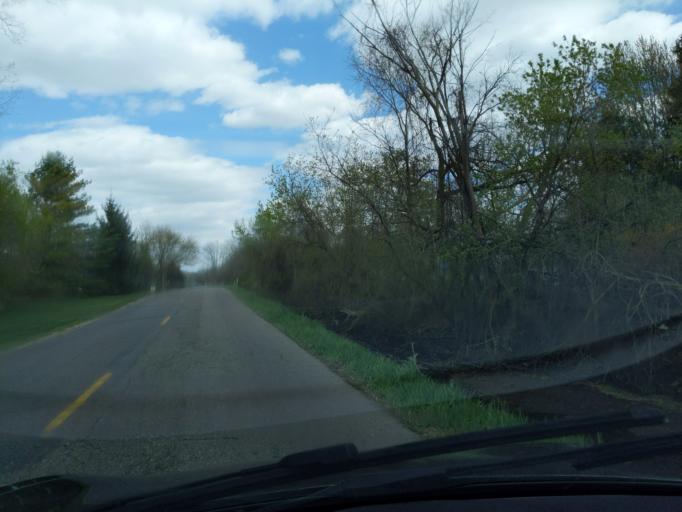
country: US
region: Michigan
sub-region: Ingham County
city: Holt
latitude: 42.6258
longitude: -84.5518
